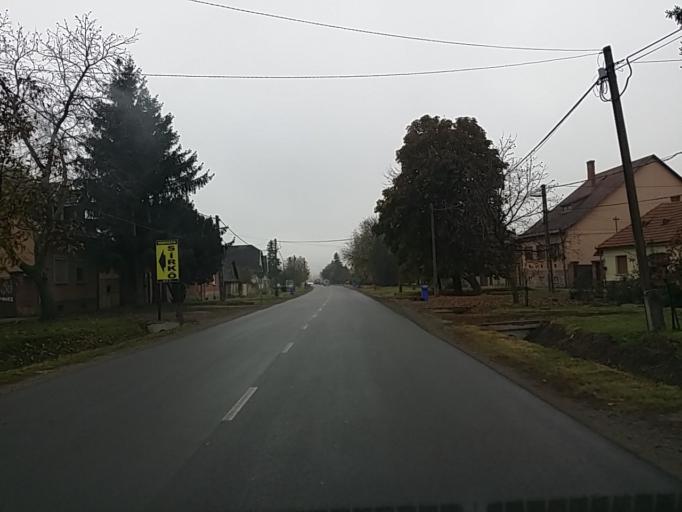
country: HU
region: Heves
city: Gyongyos
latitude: 47.7740
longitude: 19.9172
